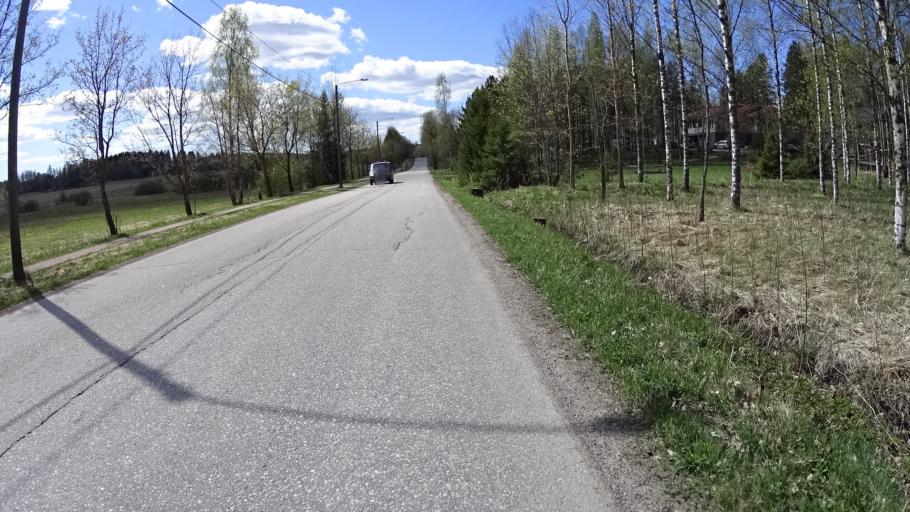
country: FI
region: Uusimaa
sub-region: Helsinki
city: Vihti
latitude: 60.3791
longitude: 24.5115
